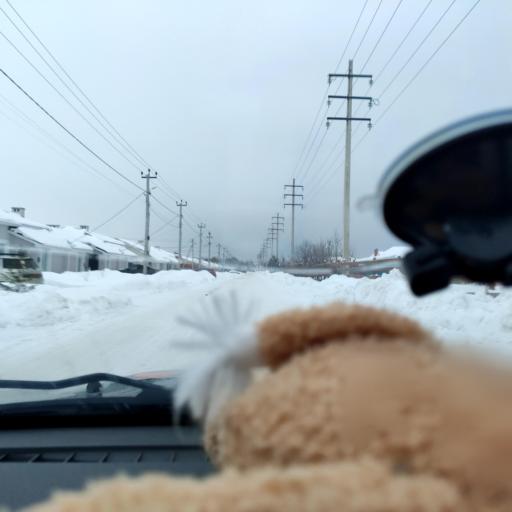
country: RU
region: Samara
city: Podstepki
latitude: 53.5771
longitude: 49.0824
